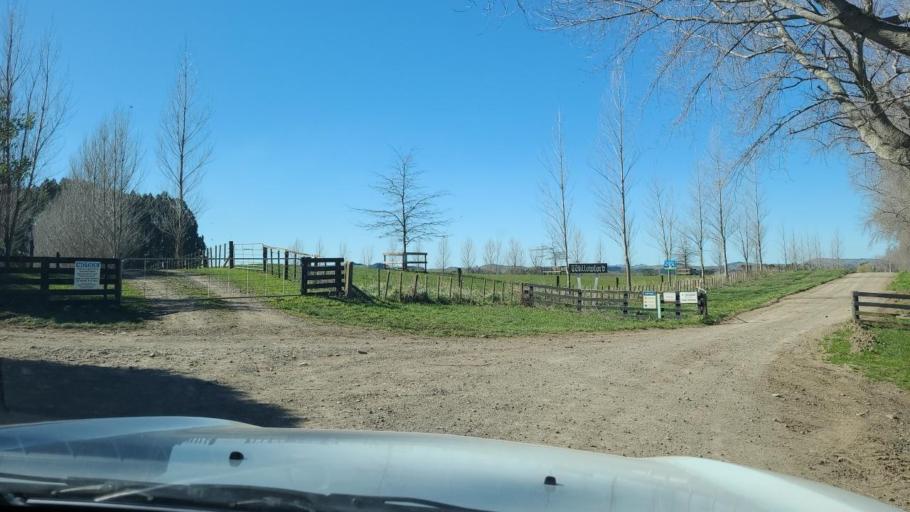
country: NZ
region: Hawke's Bay
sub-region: Napier City
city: Taradale
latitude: -39.4253
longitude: 176.5072
